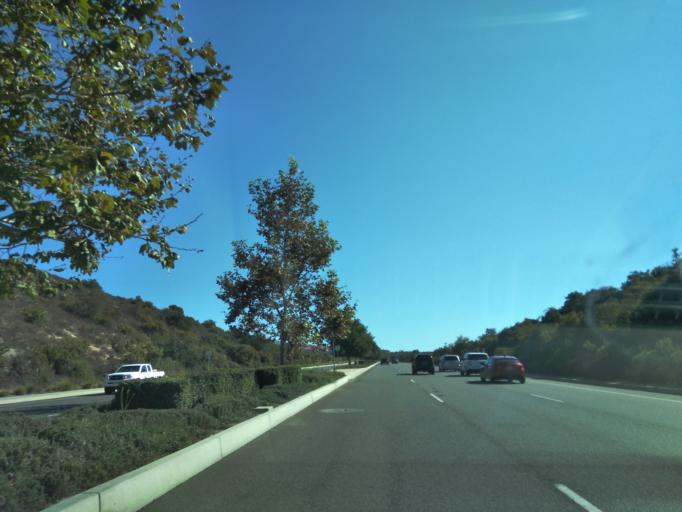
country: US
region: California
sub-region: Orange County
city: San Joaquin Hills
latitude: 33.6144
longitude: -117.8259
